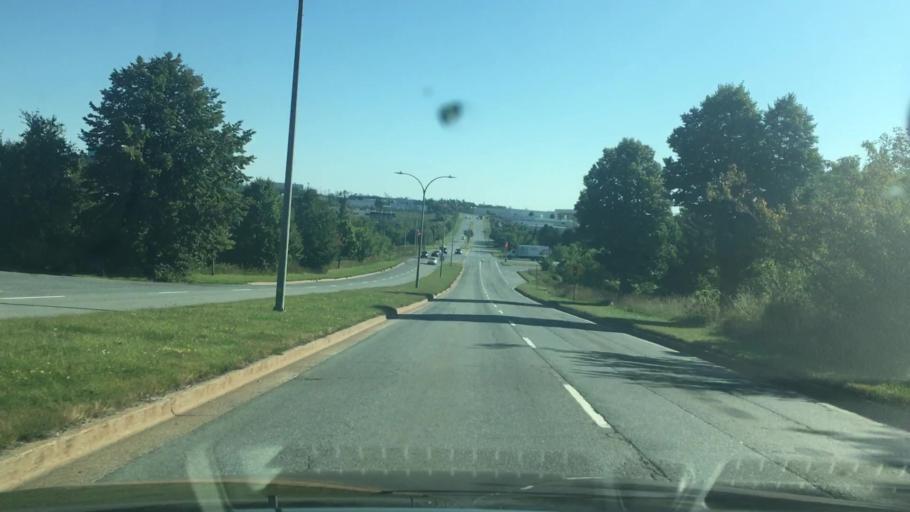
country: CA
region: Nova Scotia
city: Dartmouth
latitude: 44.7137
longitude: -63.5934
